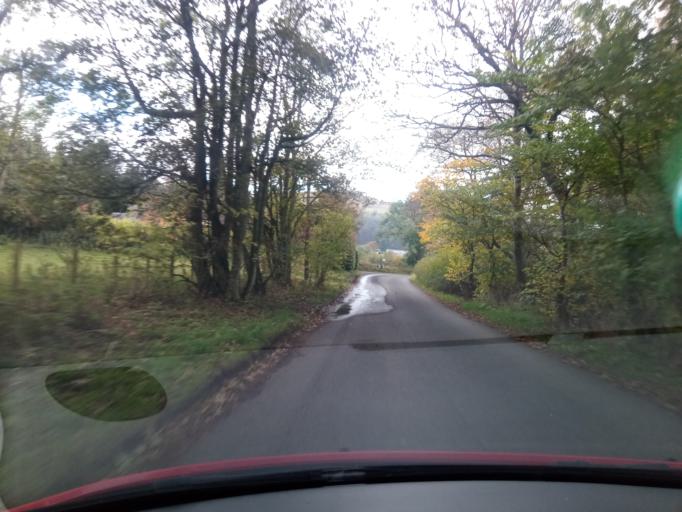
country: GB
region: Scotland
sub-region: The Scottish Borders
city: Peebles
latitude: 55.6321
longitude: -3.1383
